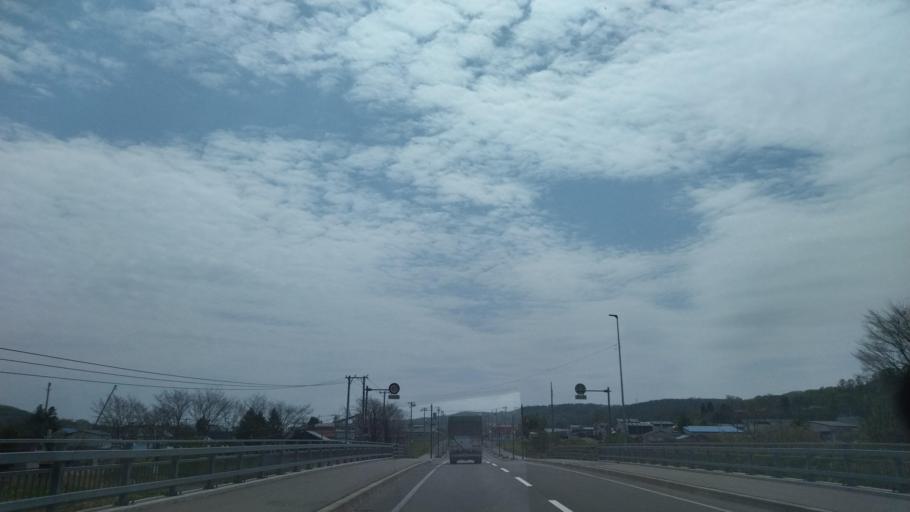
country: JP
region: Hokkaido
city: Otofuke
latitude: 43.2546
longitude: 143.5478
